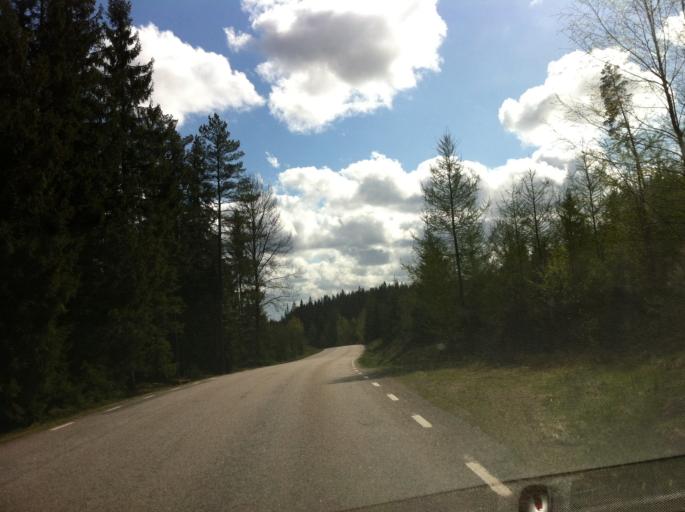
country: SE
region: Vaestra Goetaland
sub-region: Bollebygds Kommun
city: Bollebygd
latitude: 57.8125
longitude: 12.6405
